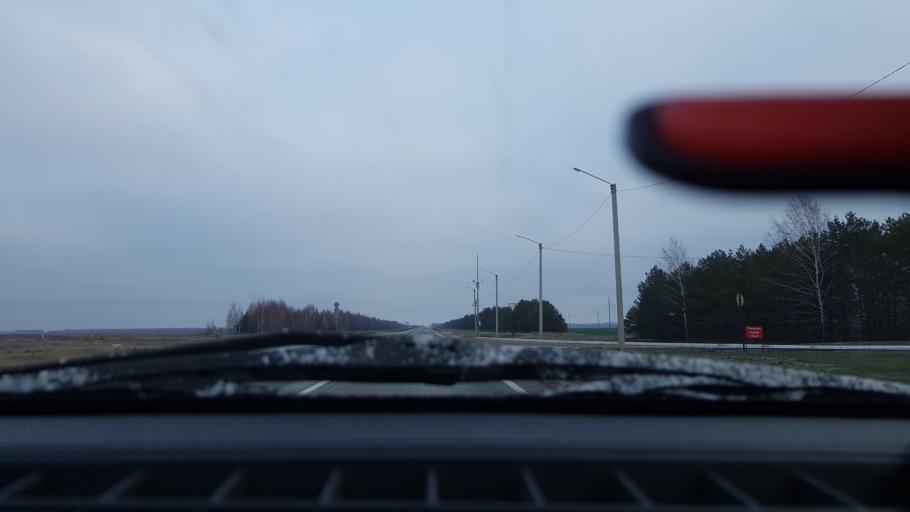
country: RU
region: Tatarstan
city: Kuybyshevskiy Zaton
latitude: 54.9541
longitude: 49.4727
